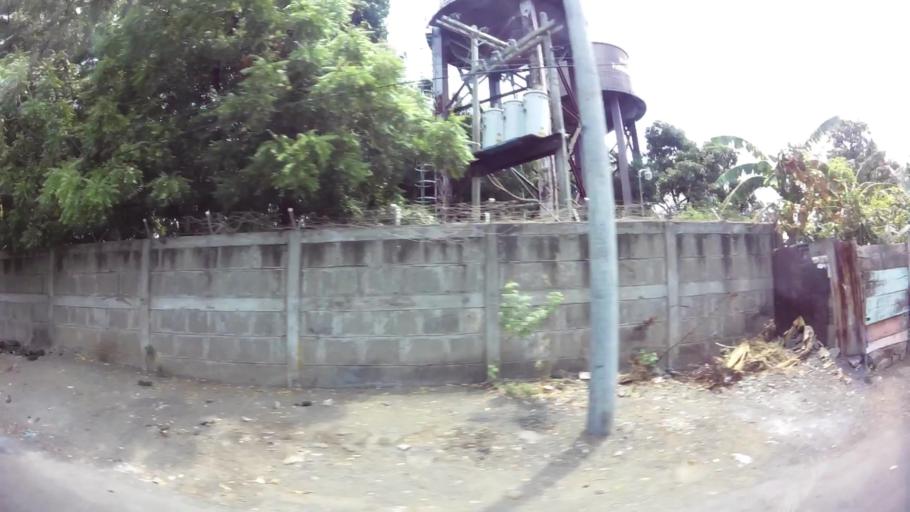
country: NI
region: Managua
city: Ciudad Sandino
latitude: 12.1287
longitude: -86.3110
